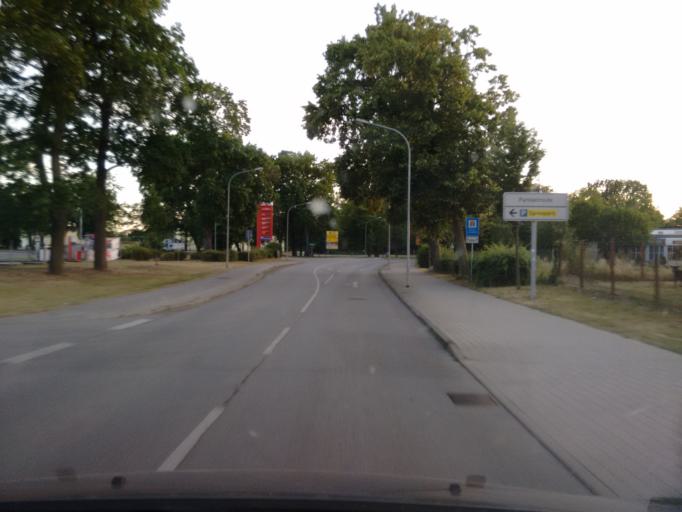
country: DE
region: Brandenburg
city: Beeskow
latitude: 52.1663
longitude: 14.2402
